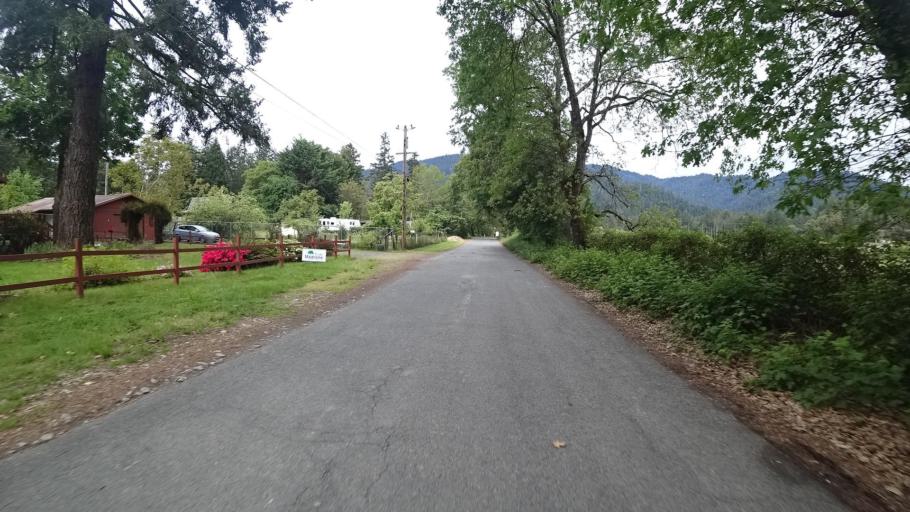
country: US
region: California
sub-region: Humboldt County
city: Willow Creek
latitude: 40.9721
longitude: -123.6289
